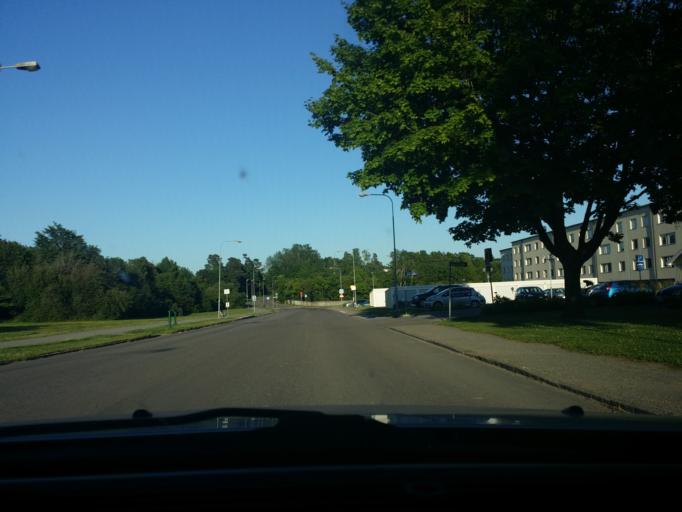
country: SE
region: Vaestmanland
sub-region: Vasteras
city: Vasteras
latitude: 59.6115
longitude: 16.5784
